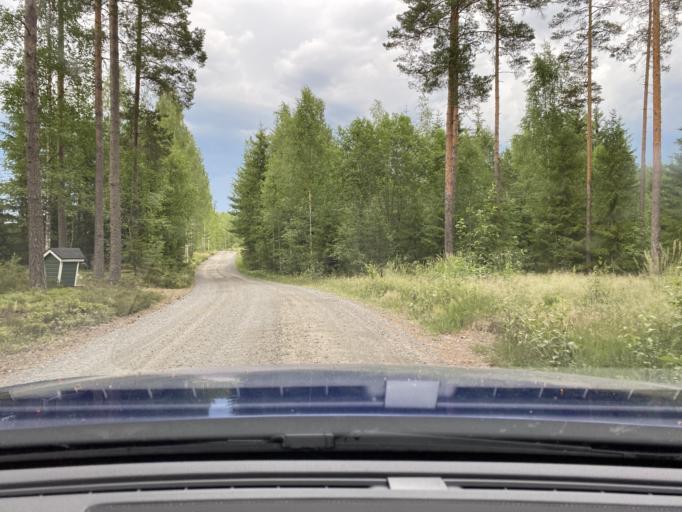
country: FI
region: Satakunta
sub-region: Rauma
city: Lappi
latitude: 61.1353
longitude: 21.9019
